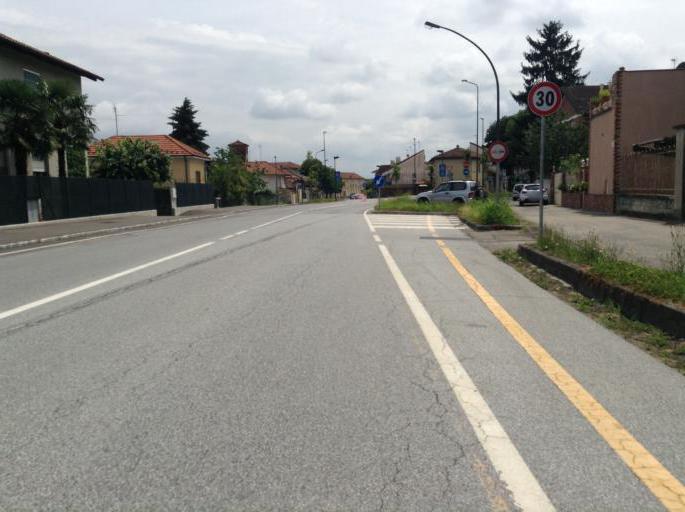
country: IT
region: Piedmont
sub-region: Provincia di Torino
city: Carignano
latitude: 44.9141
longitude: 7.6768
